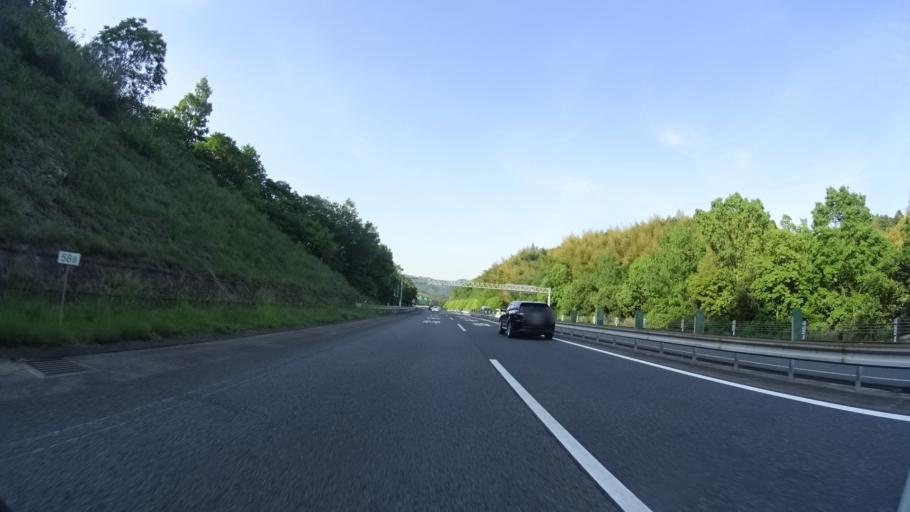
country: JP
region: Ehime
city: Kawanoecho
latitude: 33.9865
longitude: 133.5900
